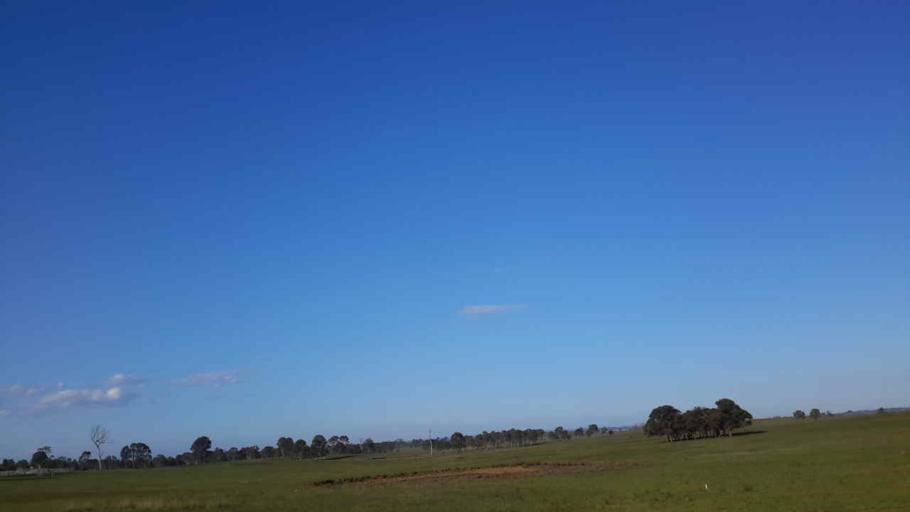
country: AU
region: New South Wales
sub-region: Liverpool
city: Luddenham
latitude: -33.8488
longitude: 150.6889
